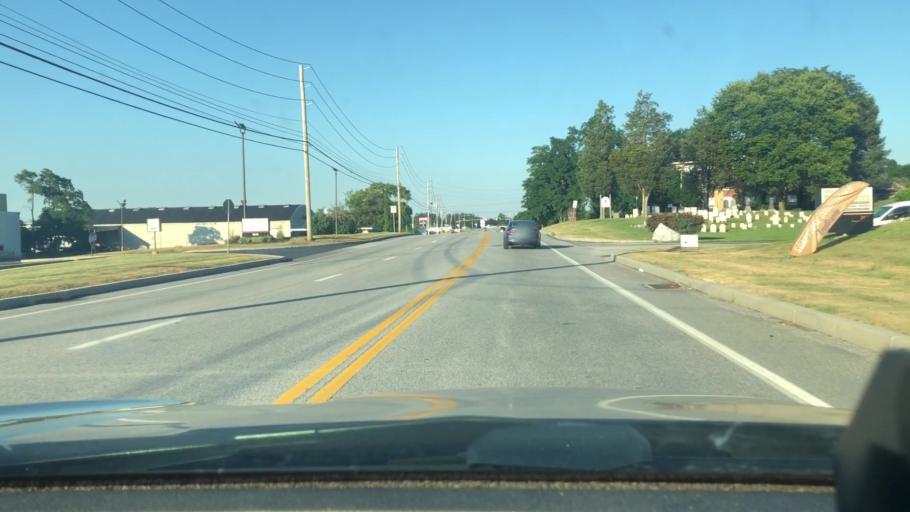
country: US
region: Pennsylvania
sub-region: Cumberland County
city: Shiremanstown
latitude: 40.2252
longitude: -76.9440
